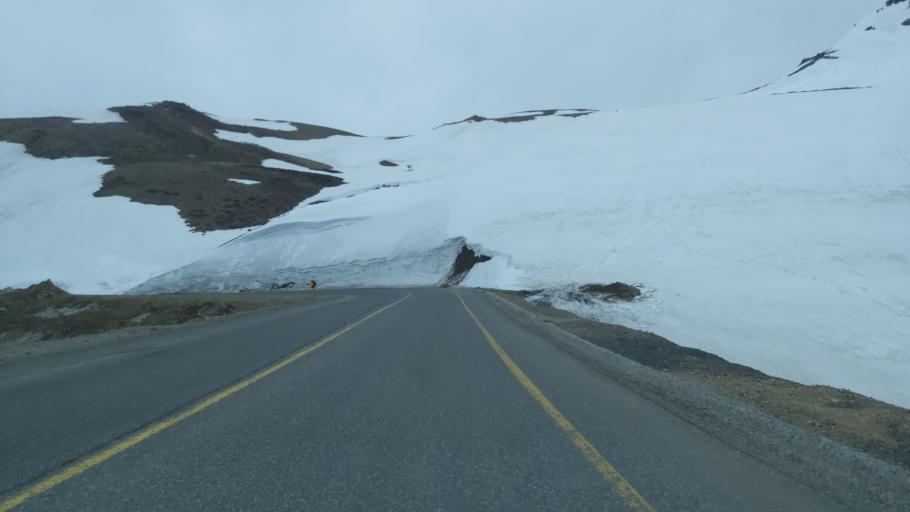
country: CL
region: Maule
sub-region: Provincia de Linares
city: Colbun
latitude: -36.0144
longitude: -70.4946
